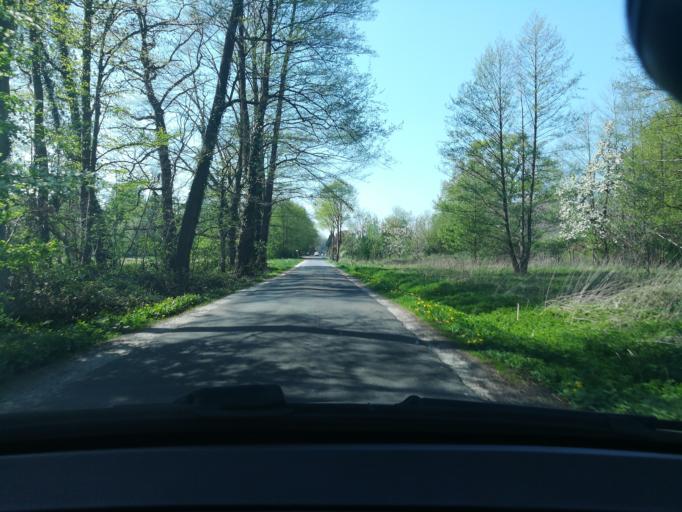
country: DE
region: North Rhine-Westphalia
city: Versmold
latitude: 52.0154
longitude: 8.1257
